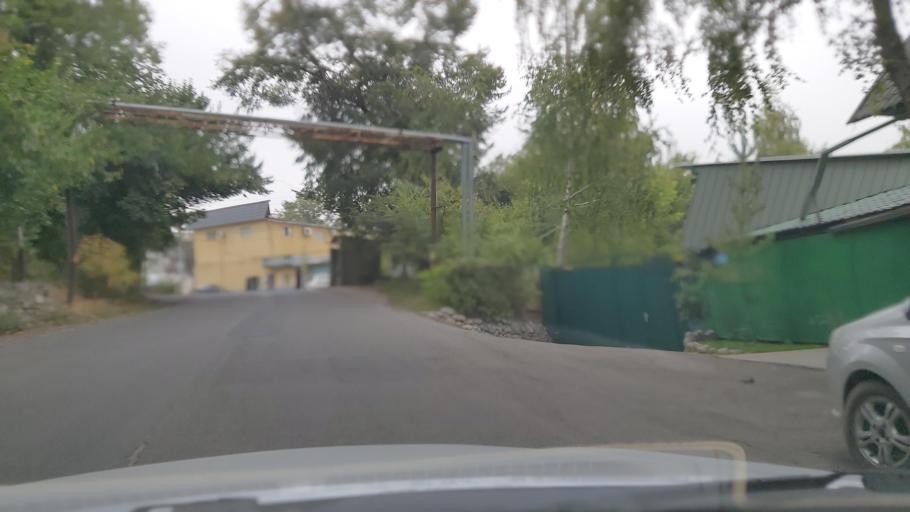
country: KZ
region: Almaty Oblysy
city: Pervomayskiy
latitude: 43.3558
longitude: 76.9786
